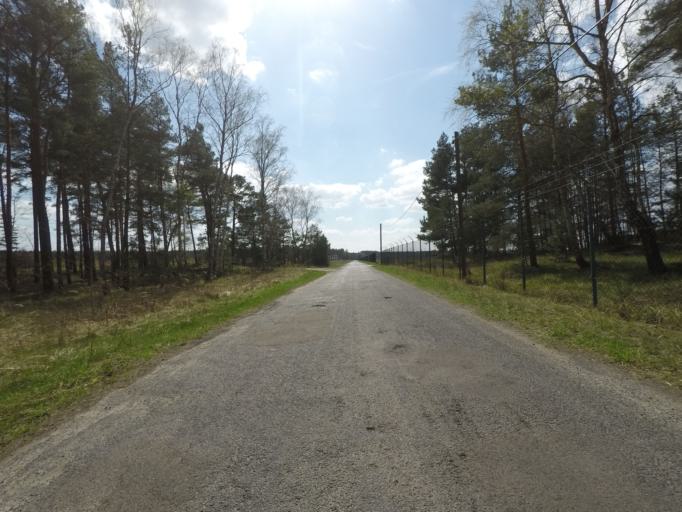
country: DE
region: Brandenburg
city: Melchow
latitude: 52.8272
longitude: 13.7190
